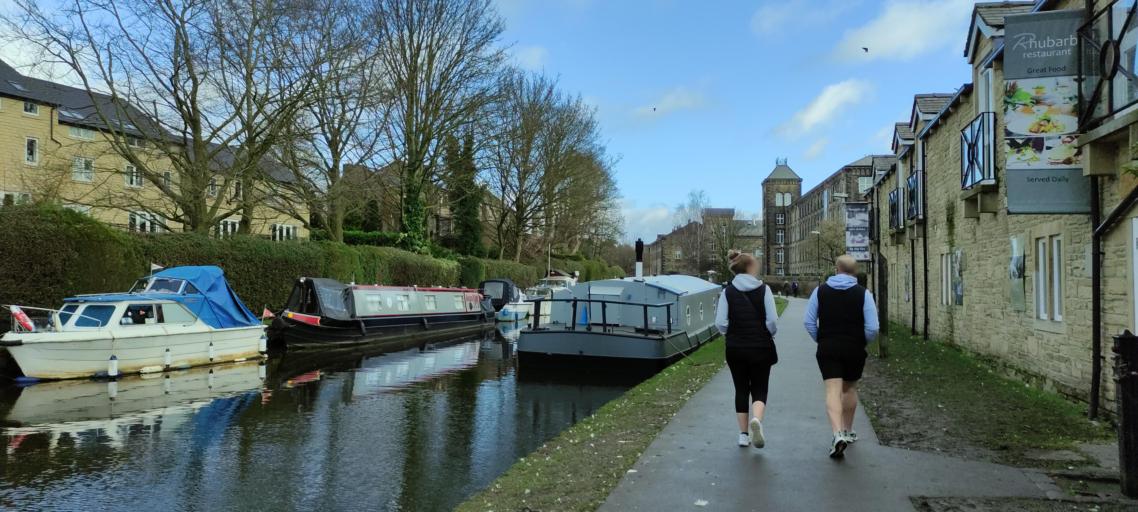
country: GB
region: England
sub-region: North Yorkshire
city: Skipton
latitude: 53.9596
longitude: -2.0262
